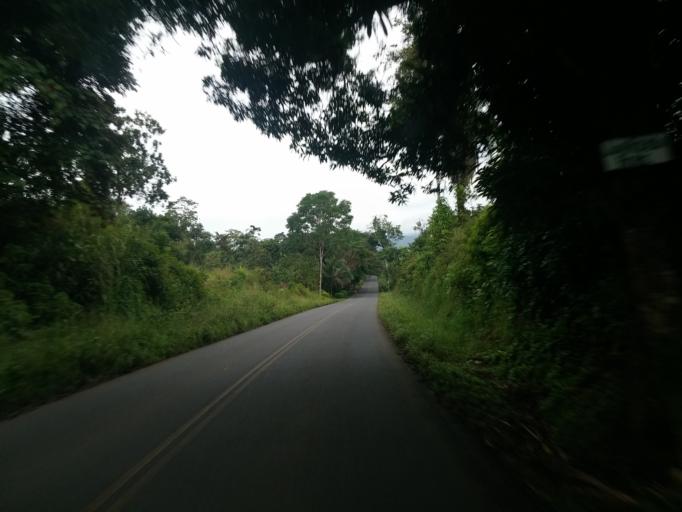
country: CR
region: Alajuela
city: Upala
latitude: 10.8474
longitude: -85.0401
